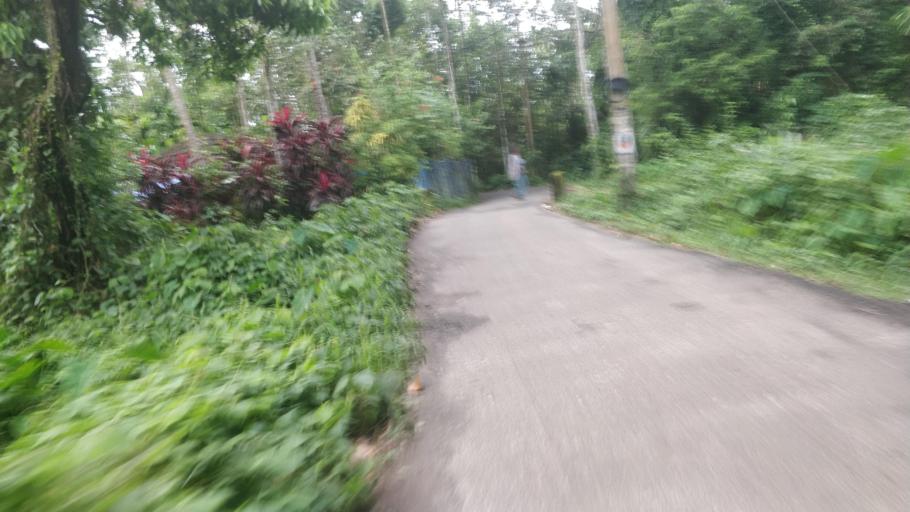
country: IN
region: Kerala
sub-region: Alappuzha
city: Shertallai
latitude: 9.6861
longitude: 76.3475
